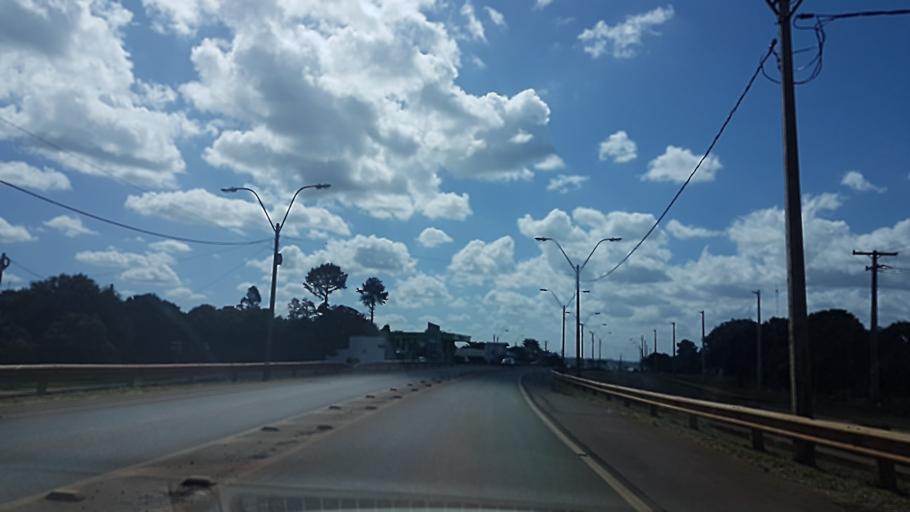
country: PY
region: Itapua
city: Carmen del Parana
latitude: -27.2192
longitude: -56.1429
